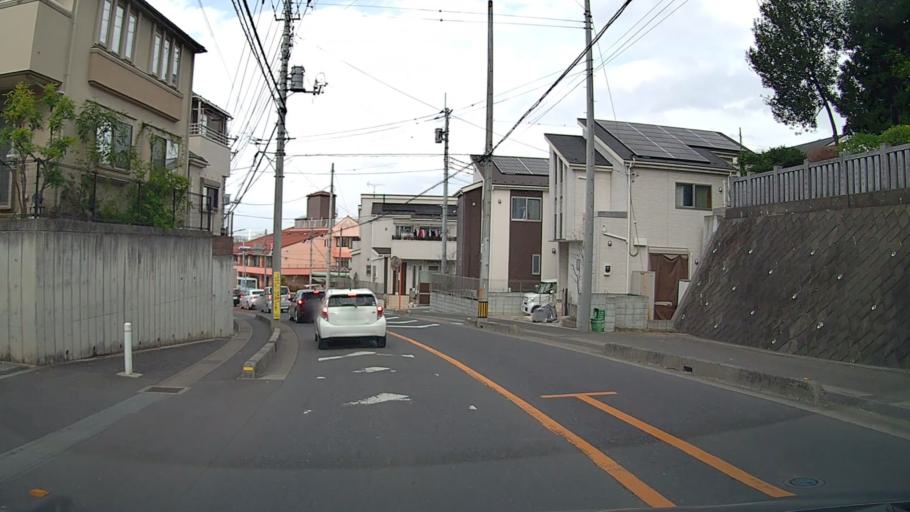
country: JP
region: Saitama
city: Shiki
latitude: 35.8278
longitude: 139.5899
